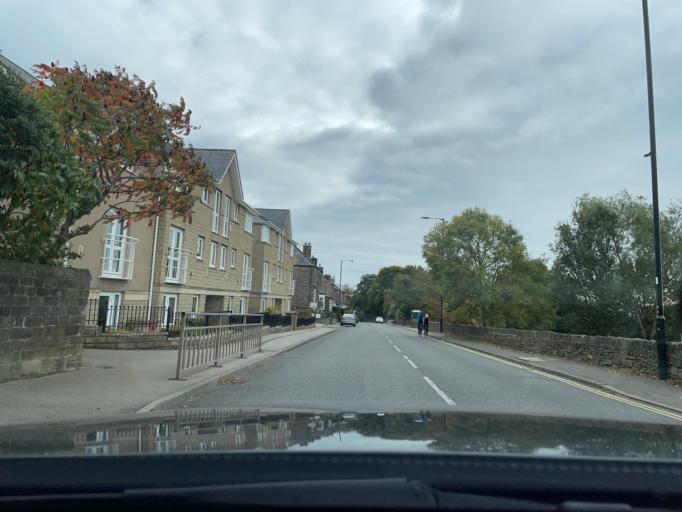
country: GB
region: England
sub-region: Sheffield
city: Sheffield
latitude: 53.3787
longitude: -1.5168
